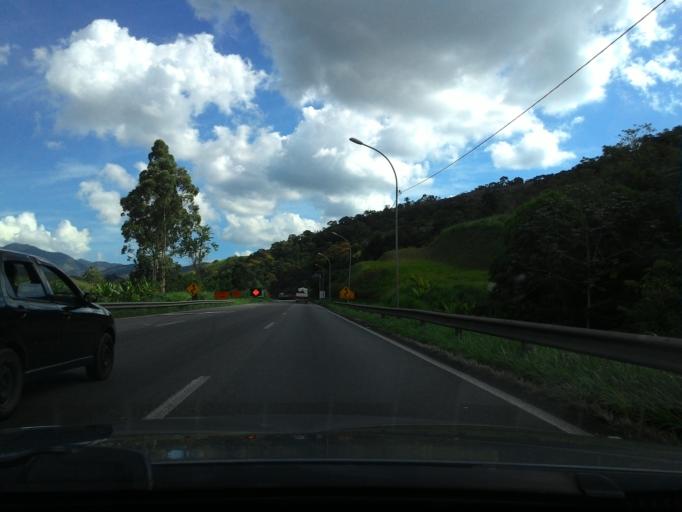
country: BR
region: Sao Paulo
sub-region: Cajati
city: Cajati
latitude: -24.8166
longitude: -48.2136
